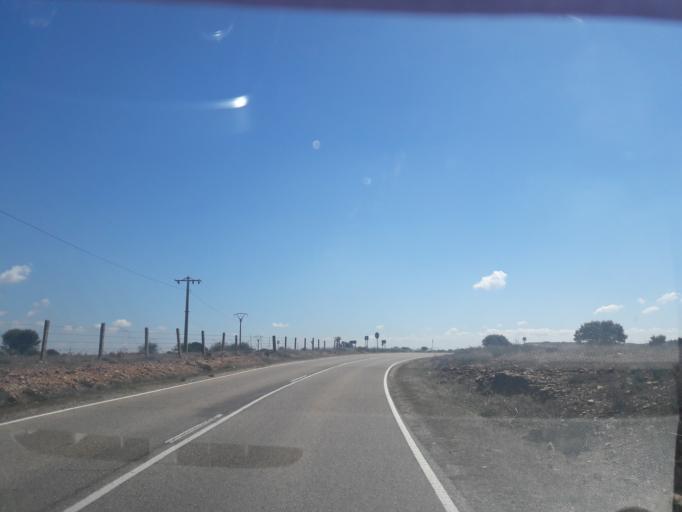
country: ES
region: Castille and Leon
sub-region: Provincia de Salamanca
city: Doninos de Salamanca
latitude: 40.9430
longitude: -5.7272
